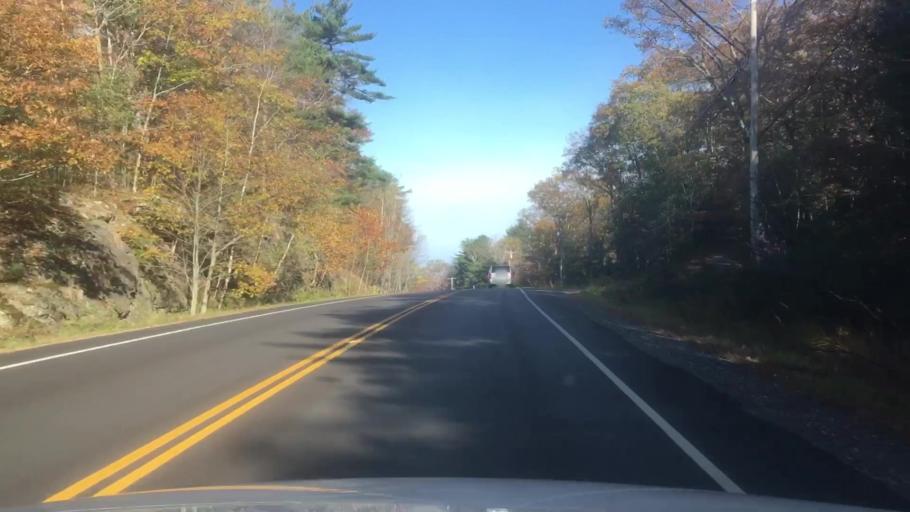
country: US
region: Maine
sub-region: Sagadahoc County
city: Woolwich
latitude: 43.8967
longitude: -69.7948
